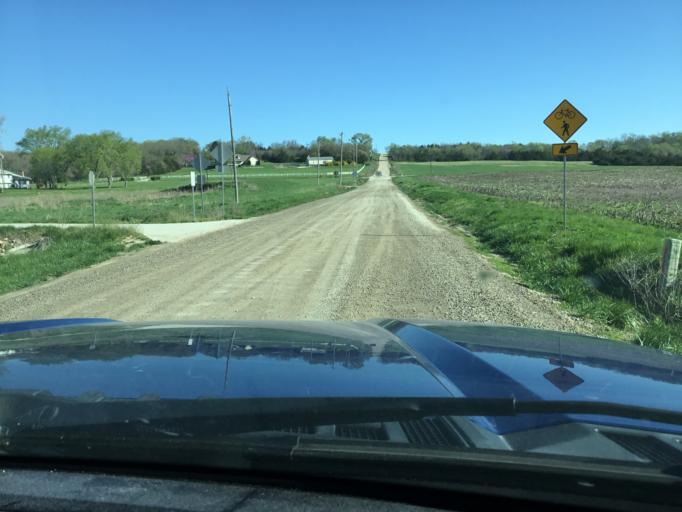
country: US
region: Kansas
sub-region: Douglas County
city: Lawrence
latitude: 38.9911
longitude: -95.3165
